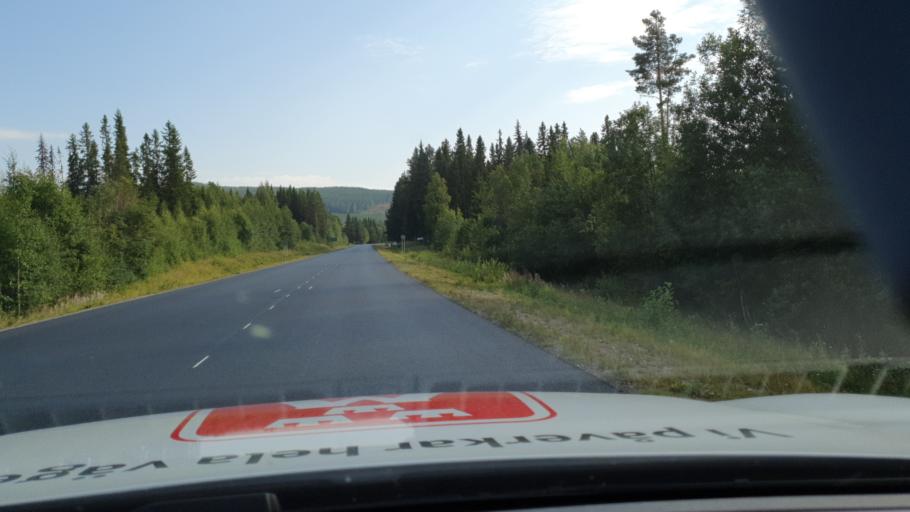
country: SE
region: Vaesterbotten
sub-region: Dorotea Kommun
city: Dorotea
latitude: 64.1906
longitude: 16.3022
